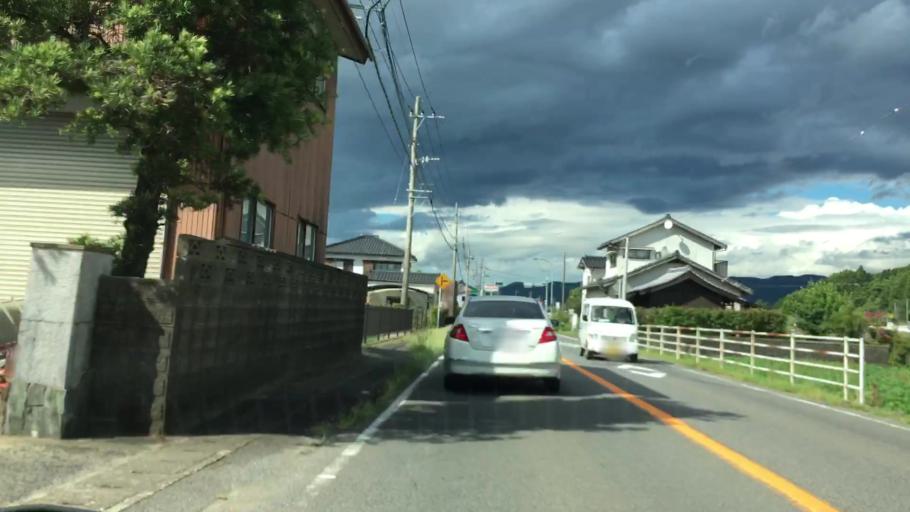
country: JP
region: Saga Prefecture
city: Imaricho-ko
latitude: 33.2505
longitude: 129.8529
